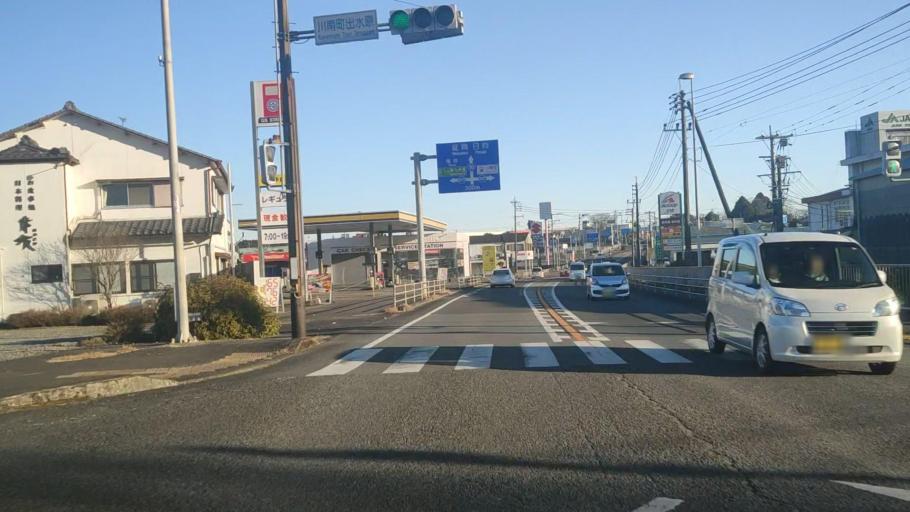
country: JP
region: Miyazaki
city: Takanabe
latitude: 32.1958
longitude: 131.5251
